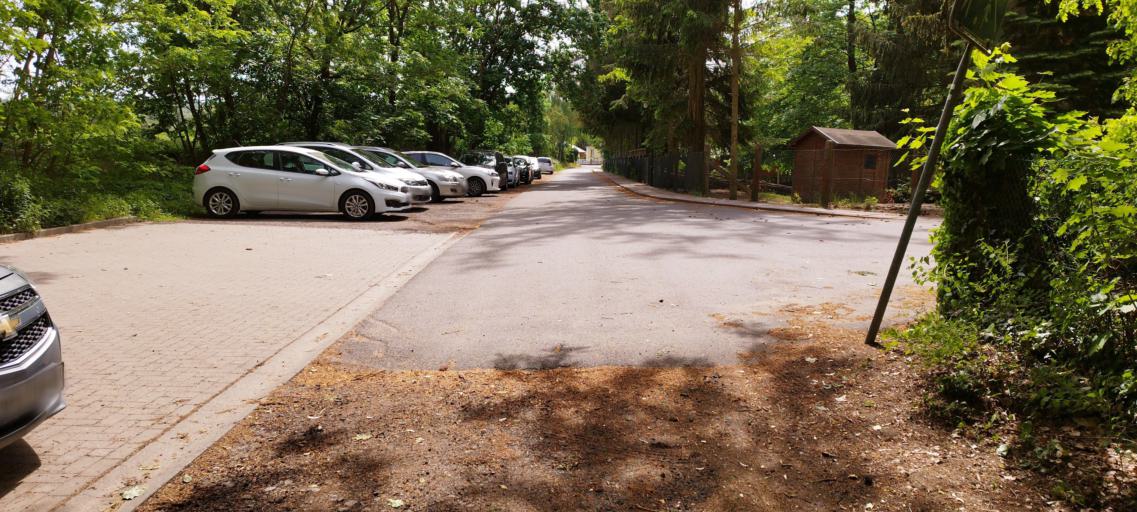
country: DE
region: Brandenburg
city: Rauen
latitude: 52.3313
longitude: 14.0184
